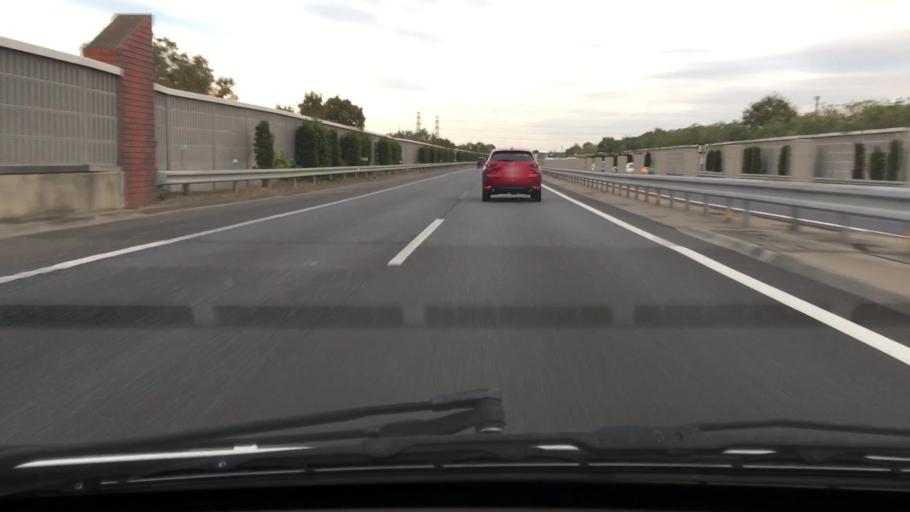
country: JP
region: Chiba
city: Ichihara
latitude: 35.5033
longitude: 140.1013
